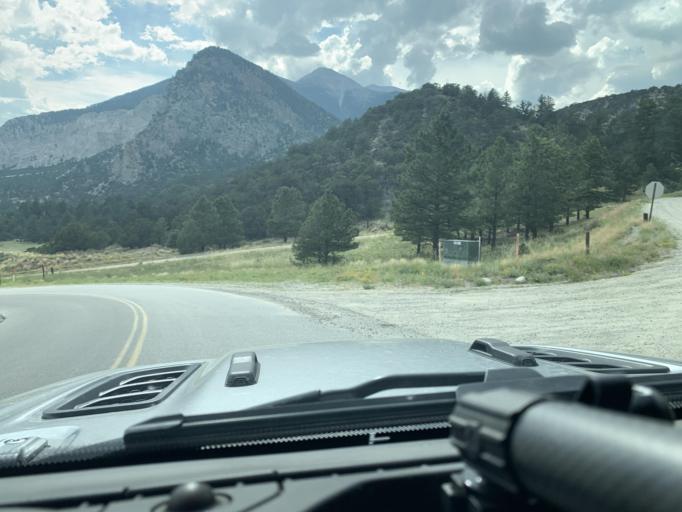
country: US
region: Colorado
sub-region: Chaffee County
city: Buena Vista
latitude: 38.7354
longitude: -106.1637
